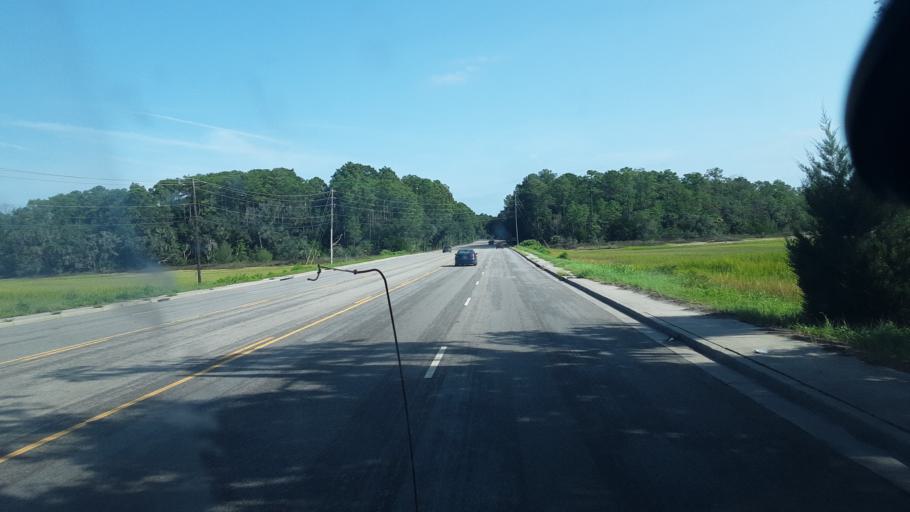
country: US
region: South Carolina
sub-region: Beaufort County
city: Burton
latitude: 32.4155
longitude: -80.7308
